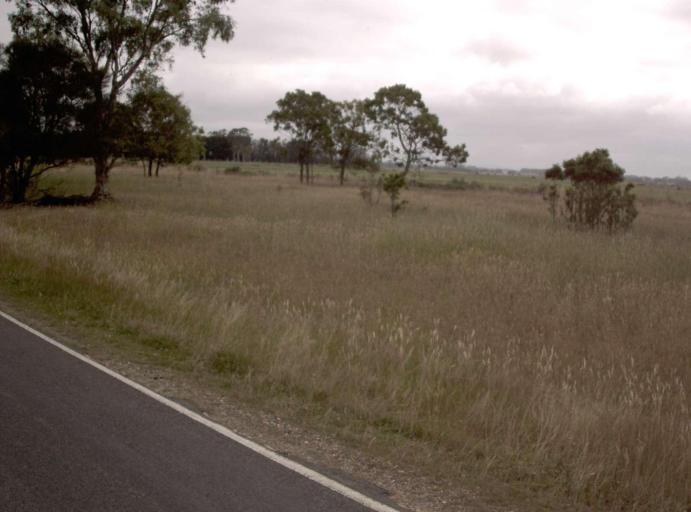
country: AU
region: Victoria
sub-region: Wellington
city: Heyfield
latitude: -38.0515
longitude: 146.7682
